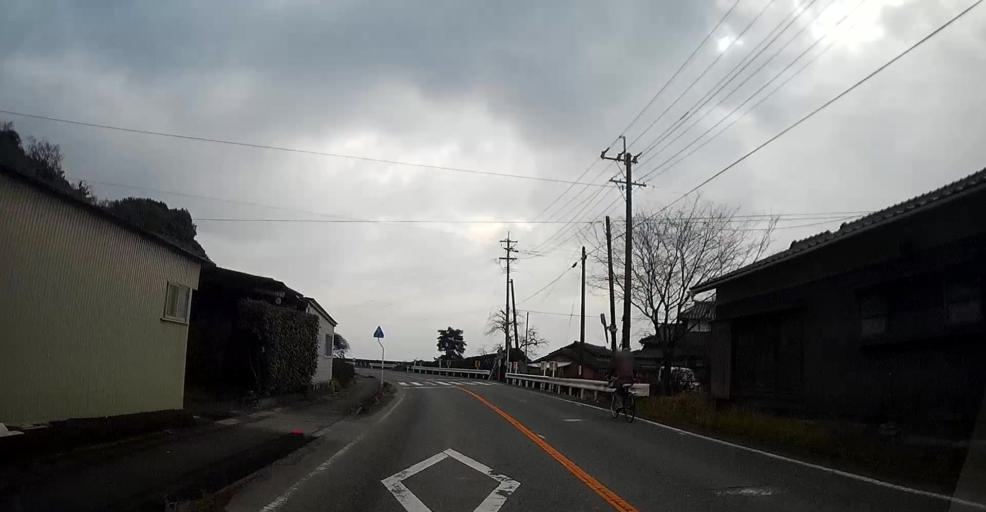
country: JP
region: Kumamoto
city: Matsubase
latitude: 32.6320
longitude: 130.6189
